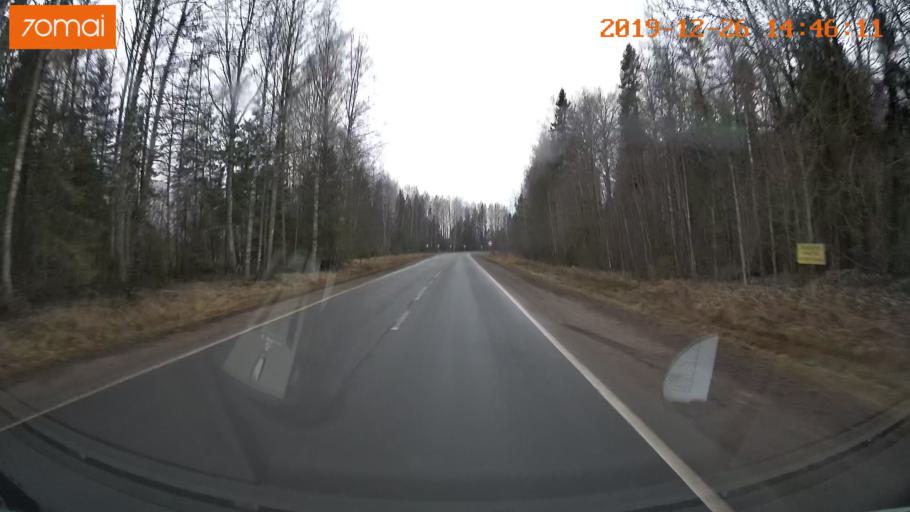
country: RU
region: Jaroslavl
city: Poshekhon'ye
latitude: 58.3348
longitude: 39.0222
